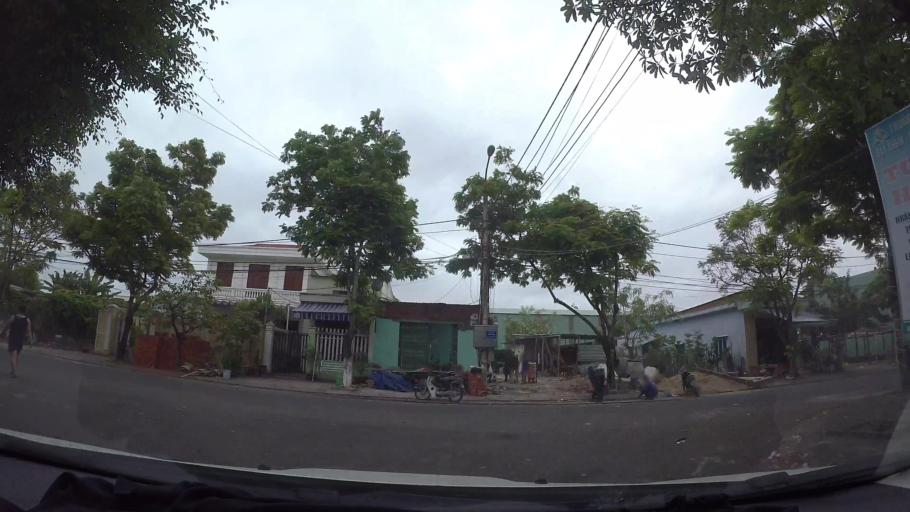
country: VN
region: Da Nang
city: Lien Chieu
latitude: 16.1244
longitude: 108.1199
